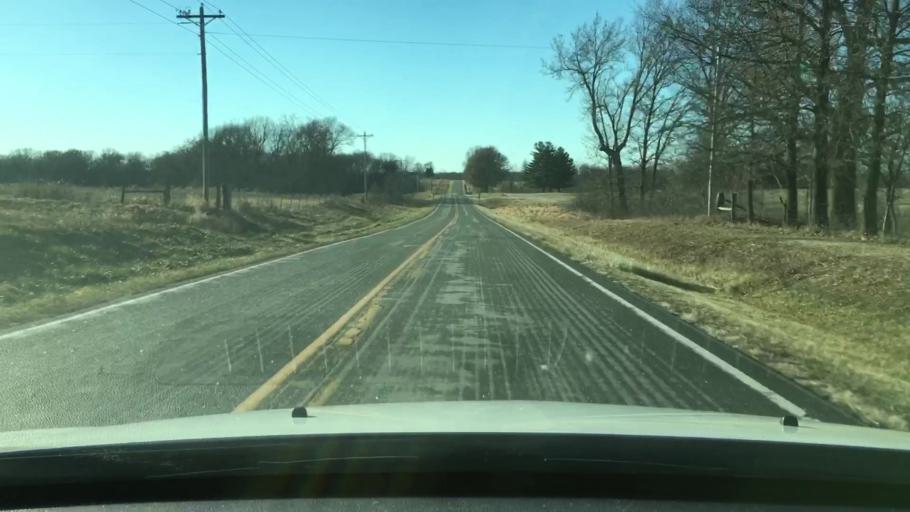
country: US
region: Missouri
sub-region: Audrain County
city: Mexico
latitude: 39.2808
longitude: -91.7579
